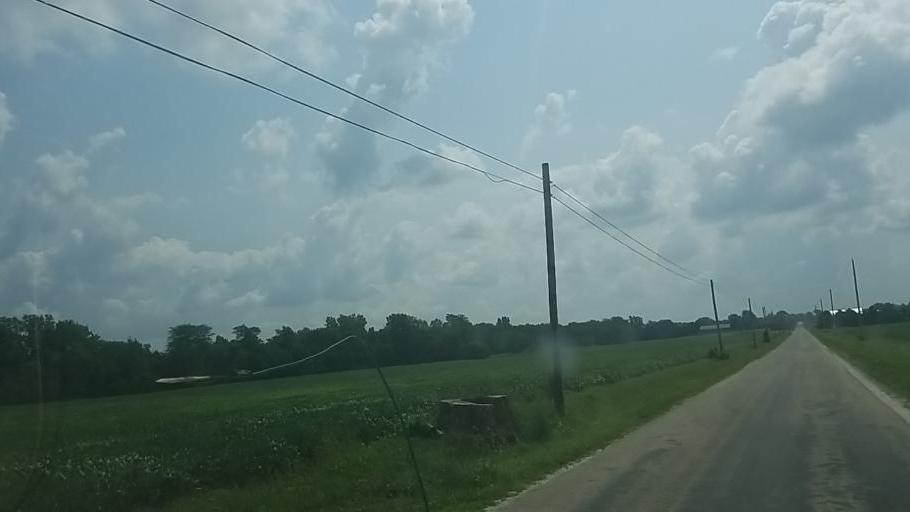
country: US
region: Ohio
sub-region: Wyandot County
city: Carey
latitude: 40.9665
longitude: -83.3337
